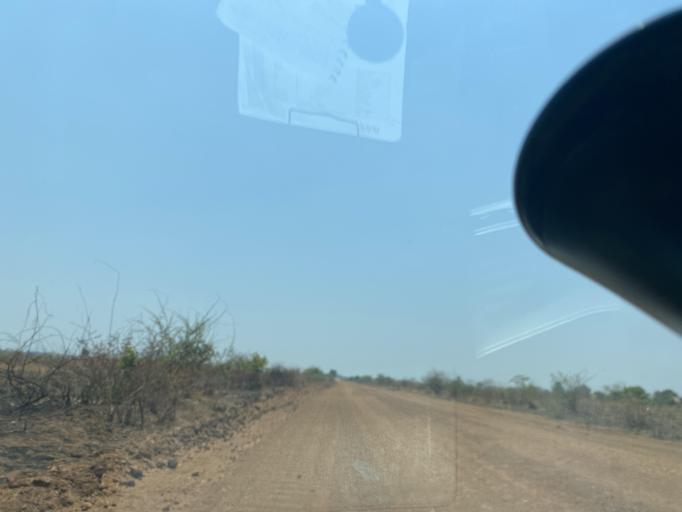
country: ZM
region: Lusaka
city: Lusaka
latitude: -15.4668
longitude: 27.9070
